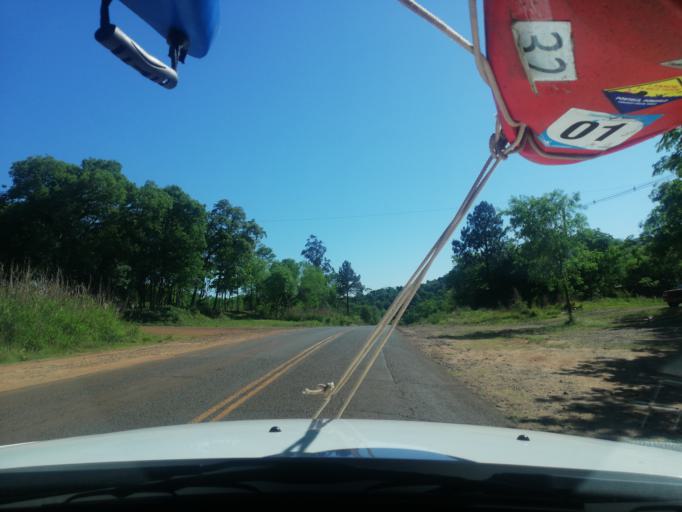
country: AR
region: Misiones
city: Santa Ana
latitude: -27.3553
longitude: -55.5861
